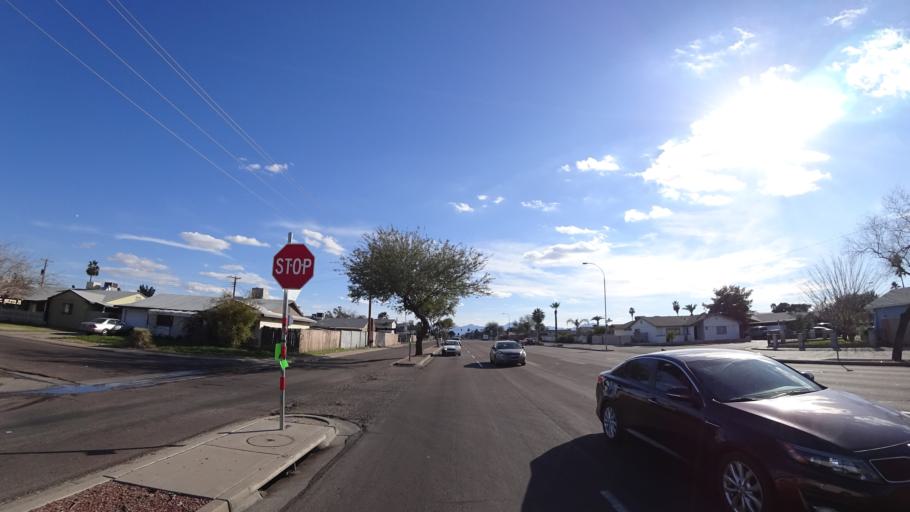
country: US
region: Arizona
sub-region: Maricopa County
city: Tolleson
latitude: 33.4891
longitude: -112.2377
